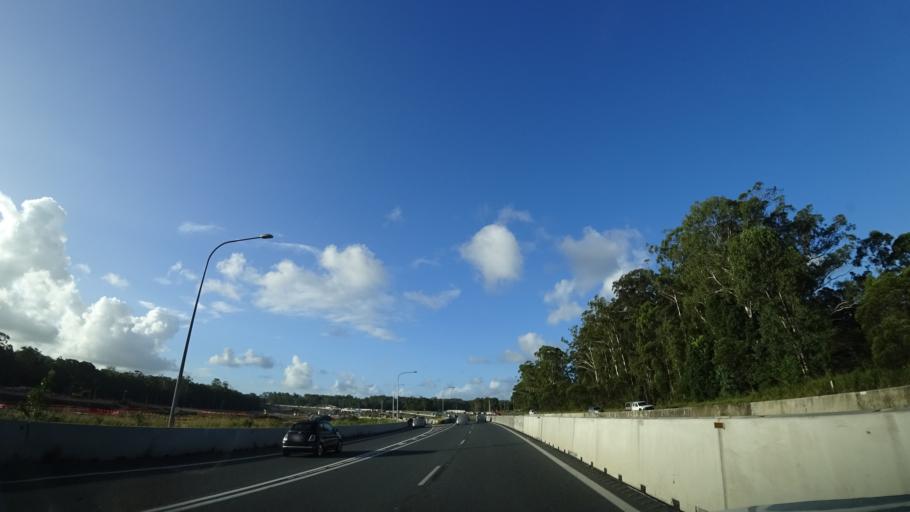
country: AU
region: Queensland
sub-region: Sunshine Coast
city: Buderim
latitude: -26.7282
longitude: 153.0463
